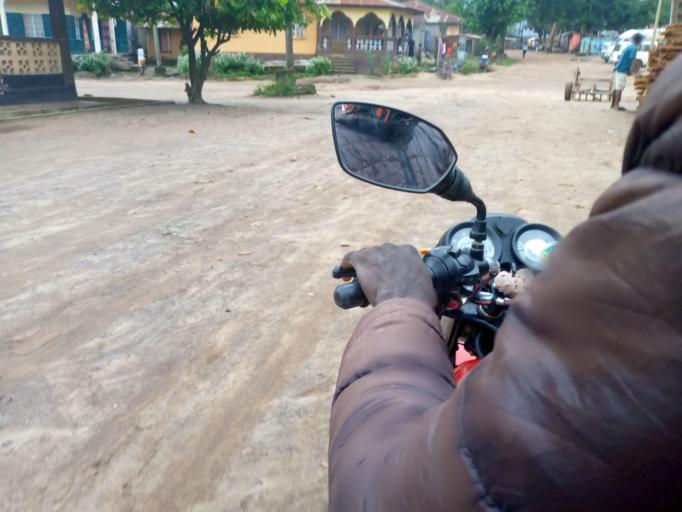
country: SL
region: Eastern Province
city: Kenema
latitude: 7.8783
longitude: -11.1867
